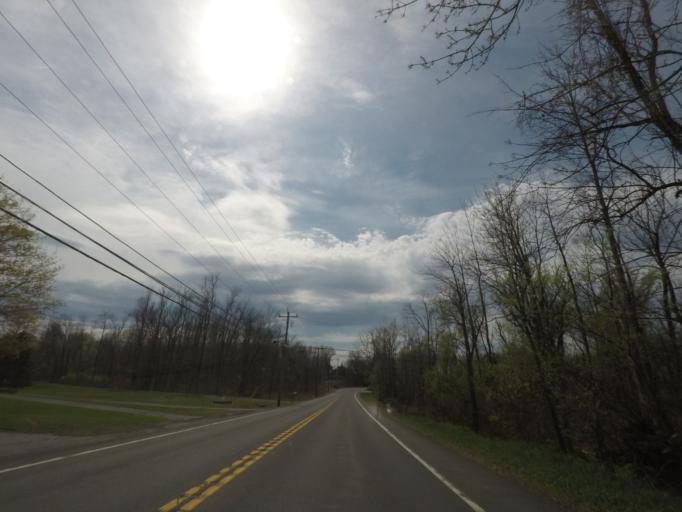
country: US
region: New York
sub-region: Columbia County
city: Philmont
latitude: 42.2964
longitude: -73.6750
